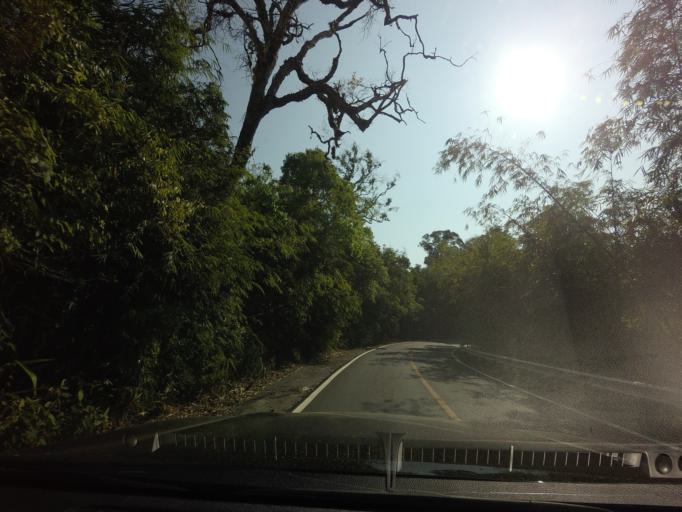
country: TH
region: Kanchanaburi
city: Thong Pha Phum
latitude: 14.6898
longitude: 98.4103
